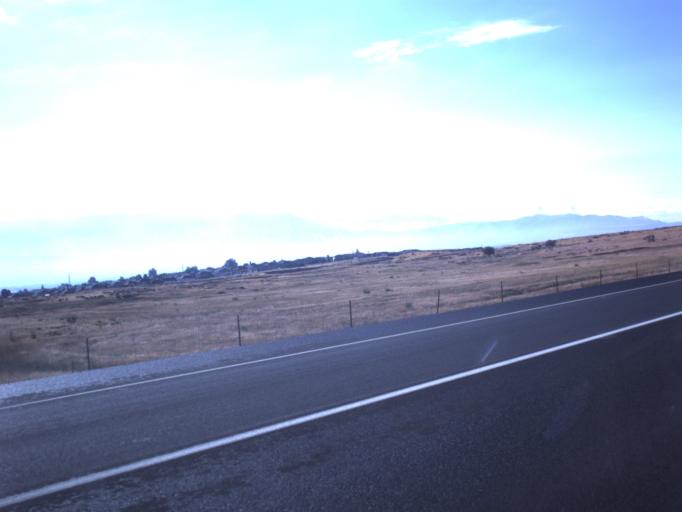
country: US
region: Utah
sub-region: Salt Lake County
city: Oquirrh
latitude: 40.6314
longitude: -112.0535
